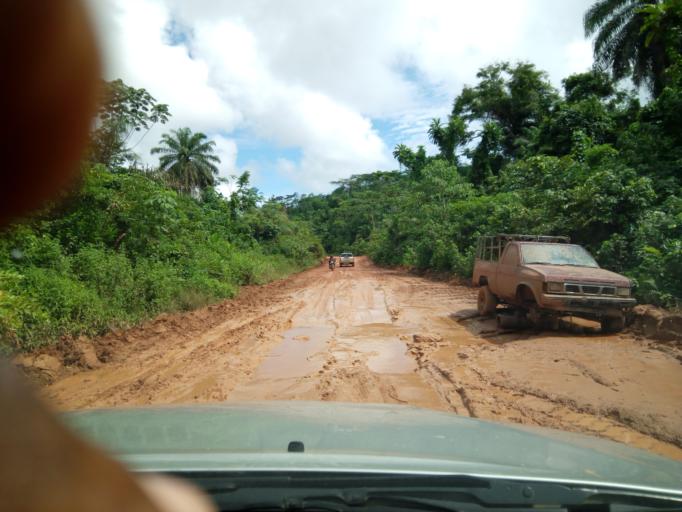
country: CI
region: Dix-Huit Montagnes
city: Toulepleu Guere
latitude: 6.7659
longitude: -8.7842
